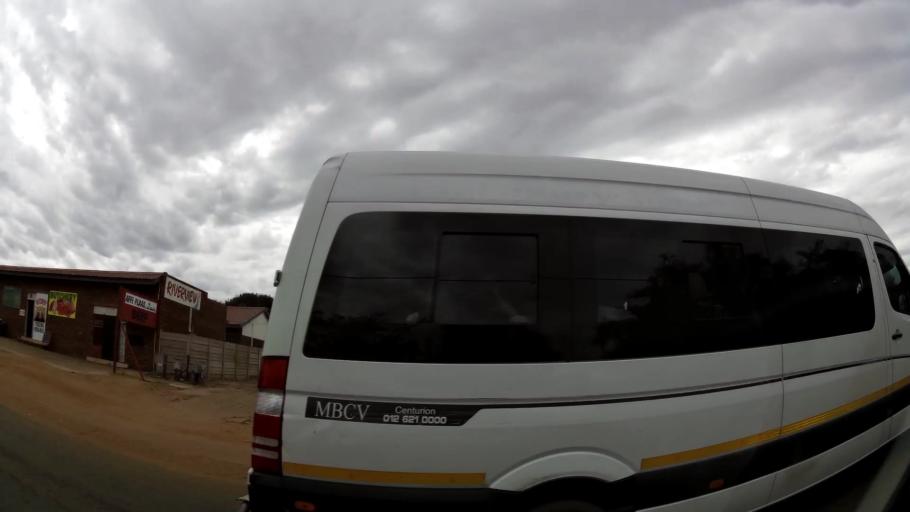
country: ZA
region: Limpopo
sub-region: Waterberg District Municipality
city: Modimolle
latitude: -24.7017
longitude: 28.4141
